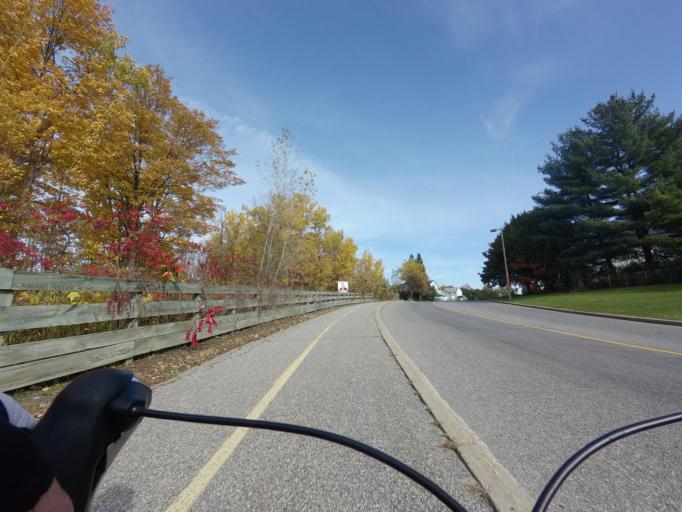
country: CA
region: Quebec
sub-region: Outaouais
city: Gatineau
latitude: 45.5068
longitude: -75.6604
